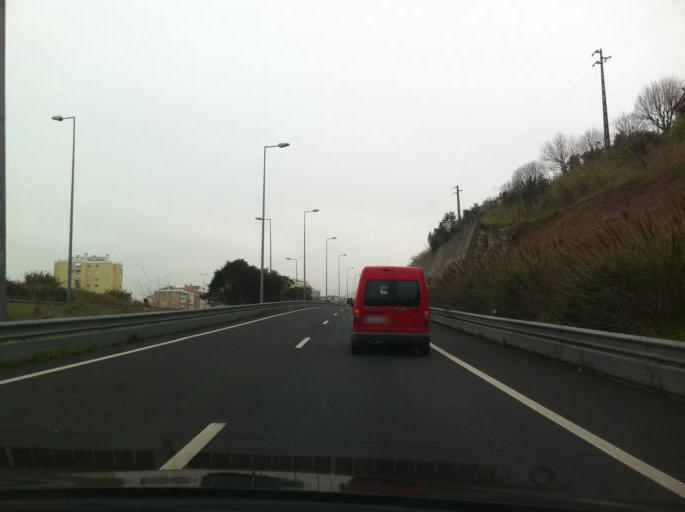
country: PT
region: Lisbon
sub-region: Odivelas
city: Pontinha
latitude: 38.7693
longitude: -9.2110
